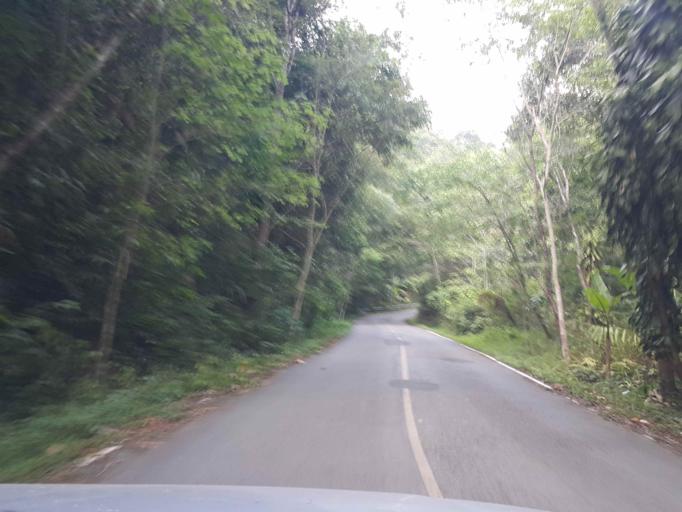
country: TH
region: Chiang Mai
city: Mae On
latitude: 18.9359
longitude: 99.3496
